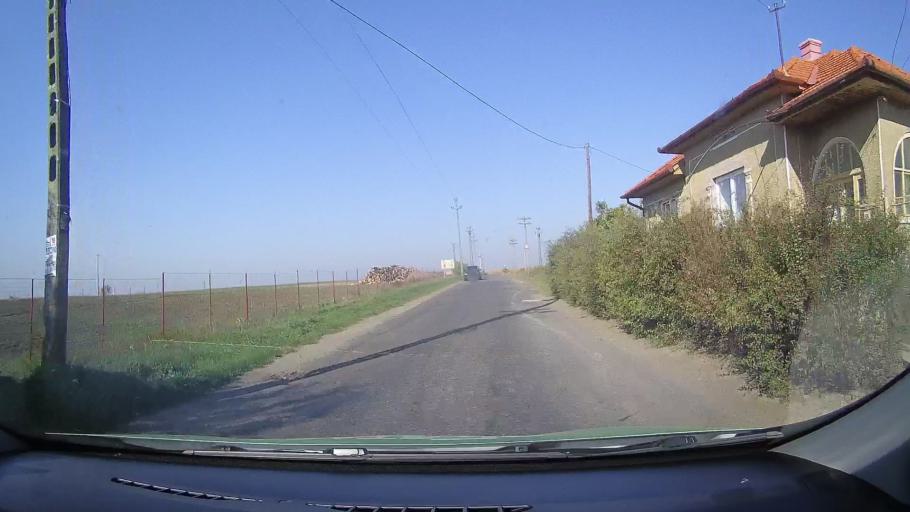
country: RO
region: Satu Mare
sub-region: Comuna Petresti
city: Petresti
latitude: 47.6093
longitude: 22.3561
